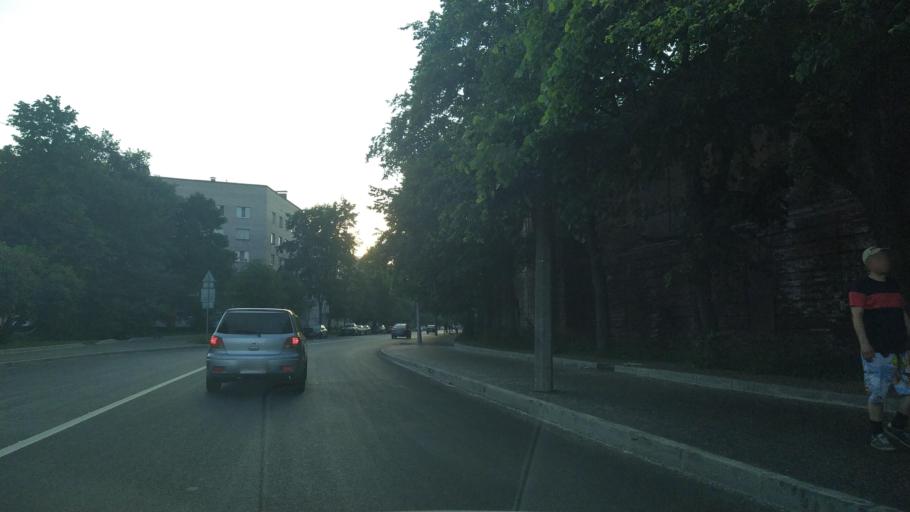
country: RU
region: St.-Petersburg
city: Kronshtadt
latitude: 59.9965
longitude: 29.7786
